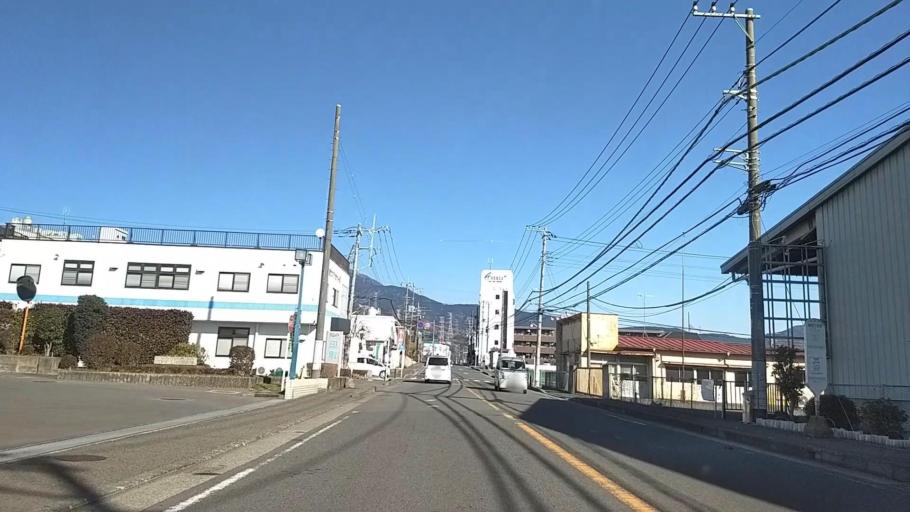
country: JP
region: Kanagawa
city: Hadano
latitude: 35.3798
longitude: 139.2113
